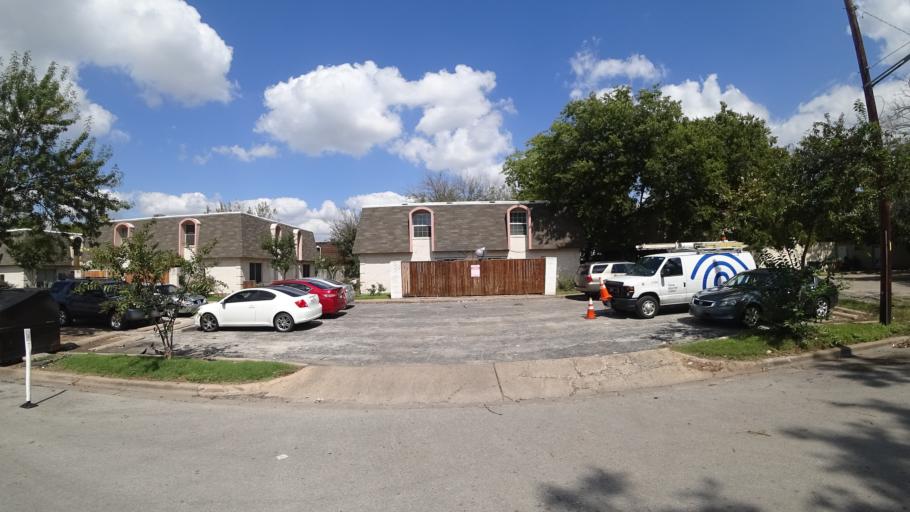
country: US
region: Texas
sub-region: Travis County
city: Wells Branch
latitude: 30.3659
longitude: -97.7220
